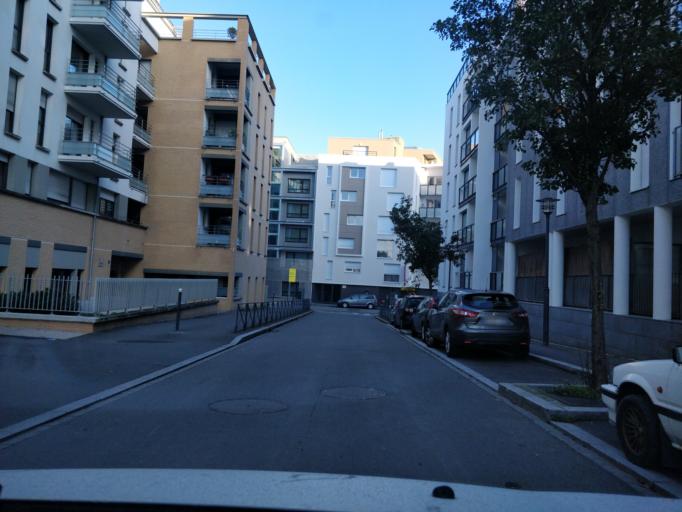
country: FR
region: Brittany
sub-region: Departement d'Ille-et-Vilaine
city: Rennes
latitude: 48.1048
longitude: -1.6686
